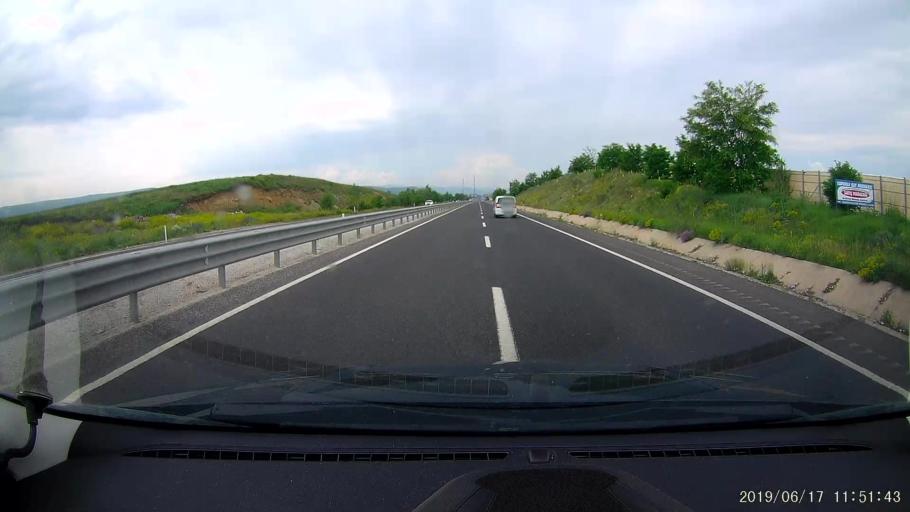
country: TR
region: Cankiri
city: Atkaracalar
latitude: 40.8158
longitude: 33.0994
